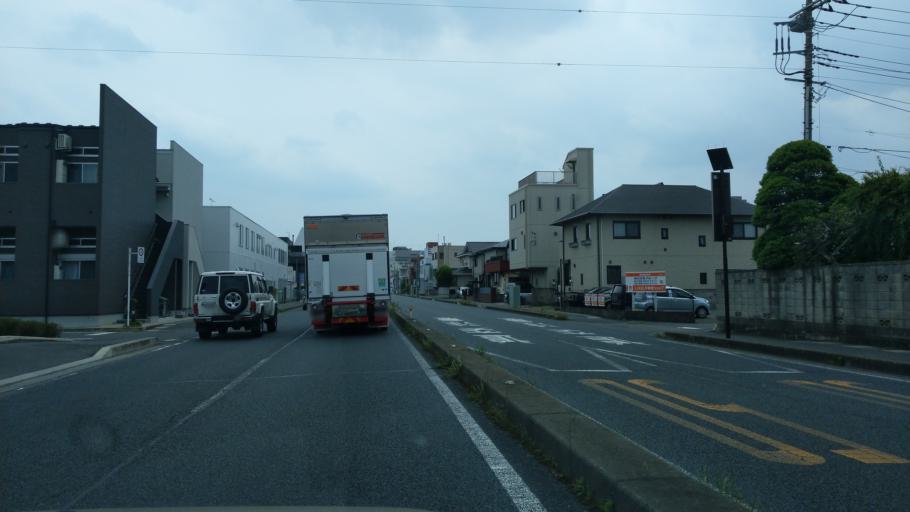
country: JP
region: Saitama
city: Ageoshimo
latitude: 35.9452
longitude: 139.6114
